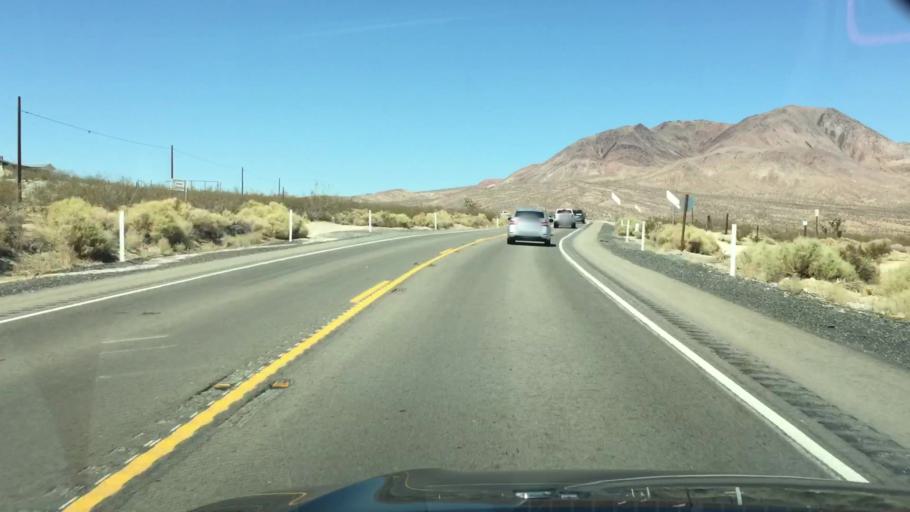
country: US
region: California
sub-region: Kern County
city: Ridgecrest
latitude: 35.3143
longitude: -117.6092
